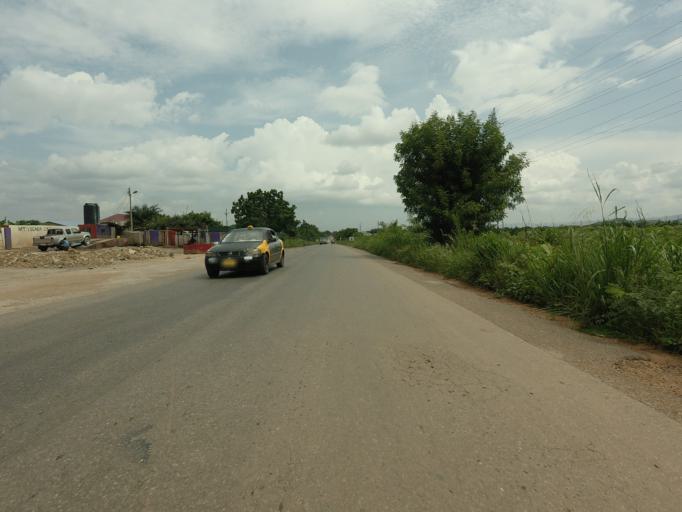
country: GH
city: Akropong
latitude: 6.1854
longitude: 0.0736
